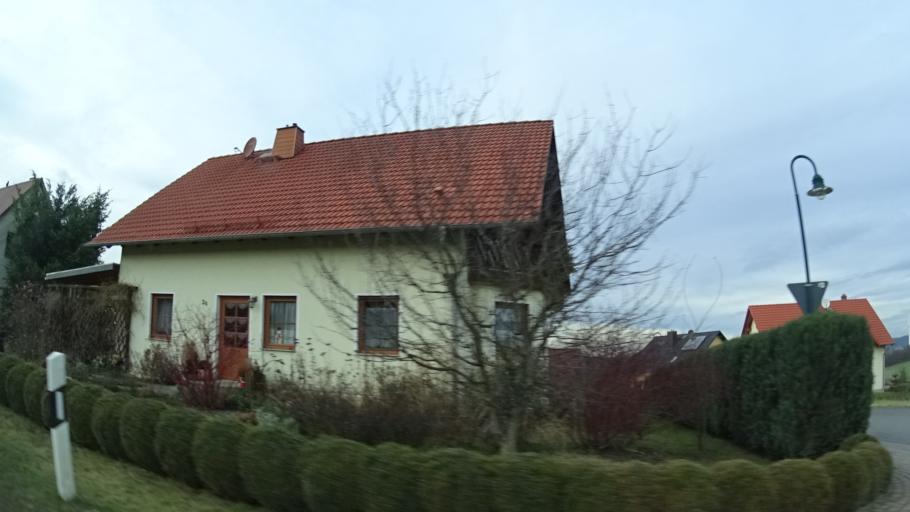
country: DE
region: Thuringia
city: Weira
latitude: 50.7048
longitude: 11.7192
